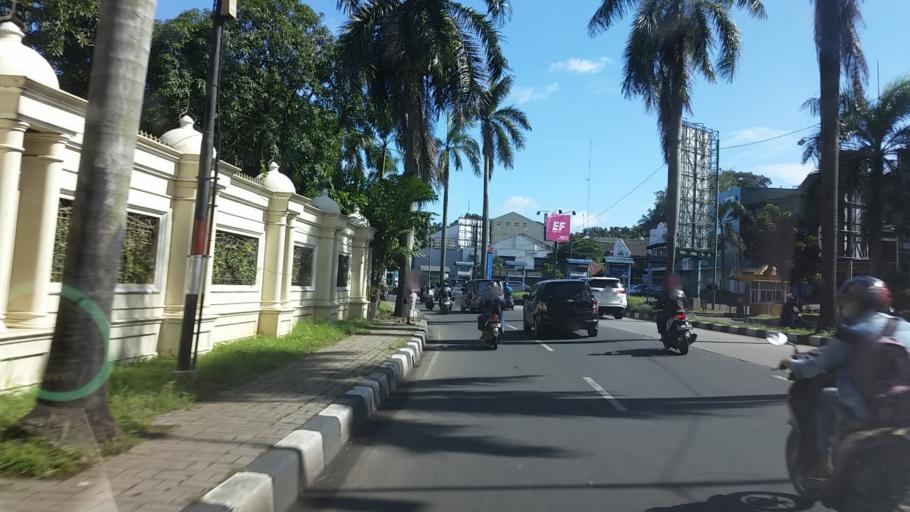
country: ID
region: Banten
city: South Tangerang
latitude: -6.2867
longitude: 106.7799
